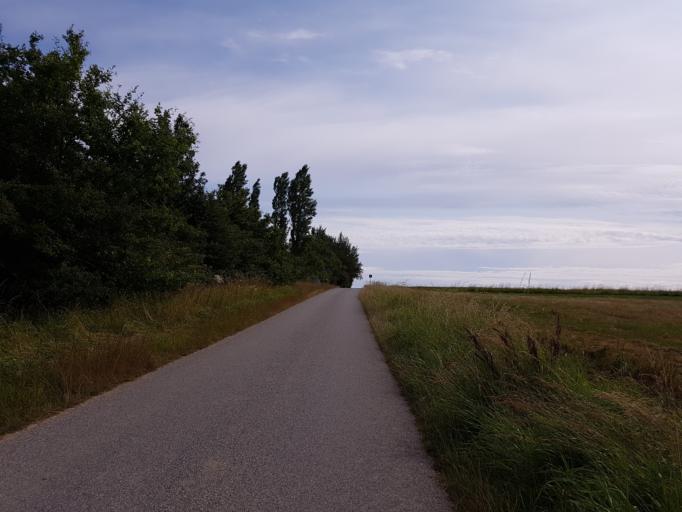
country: DK
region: Zealand
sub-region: Guldborgsund Kommune
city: Nykobing Falster
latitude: 54.5734
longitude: 11.9686
